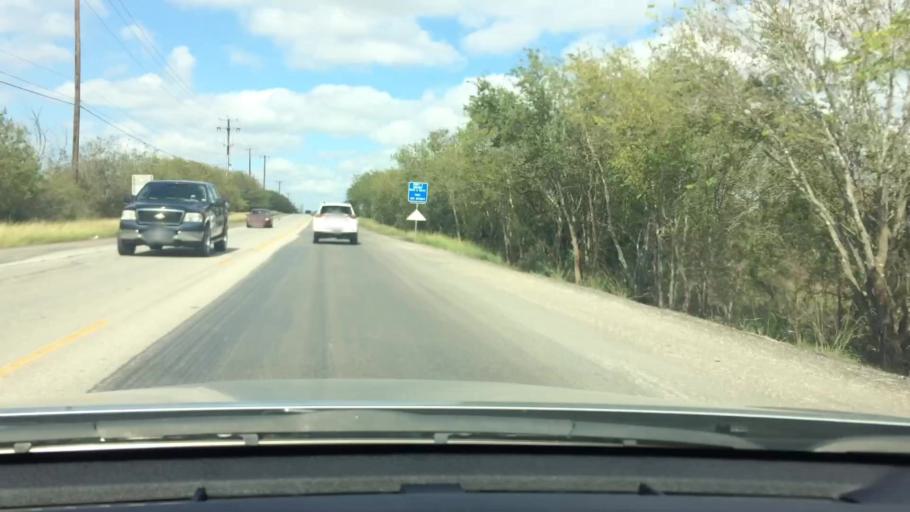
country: US
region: Texas
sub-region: Bexar County
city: Converse
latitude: 29.4814
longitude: -98.3128
